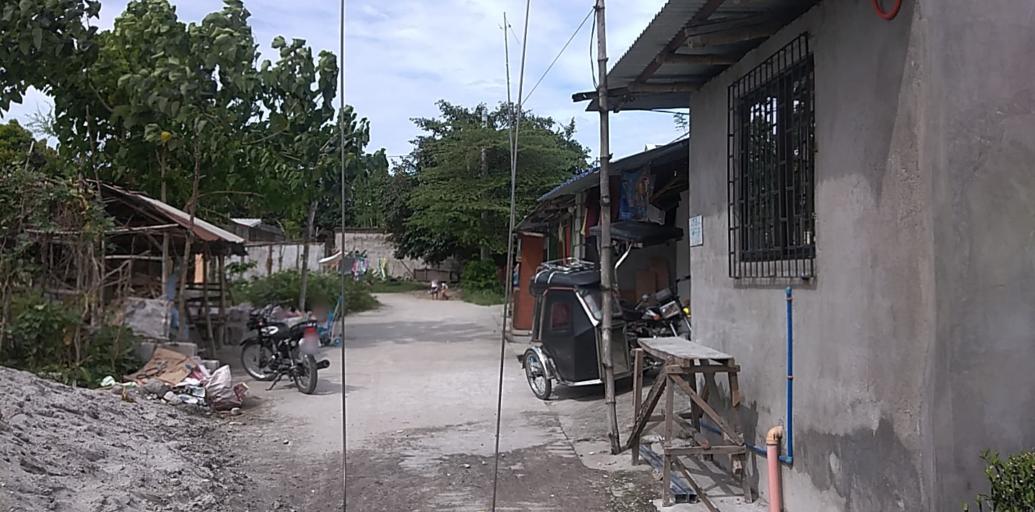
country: PH
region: Central Luzon
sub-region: Province of Pampanga
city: Manibaug Pasig
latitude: 15.1138
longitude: 120.5583
